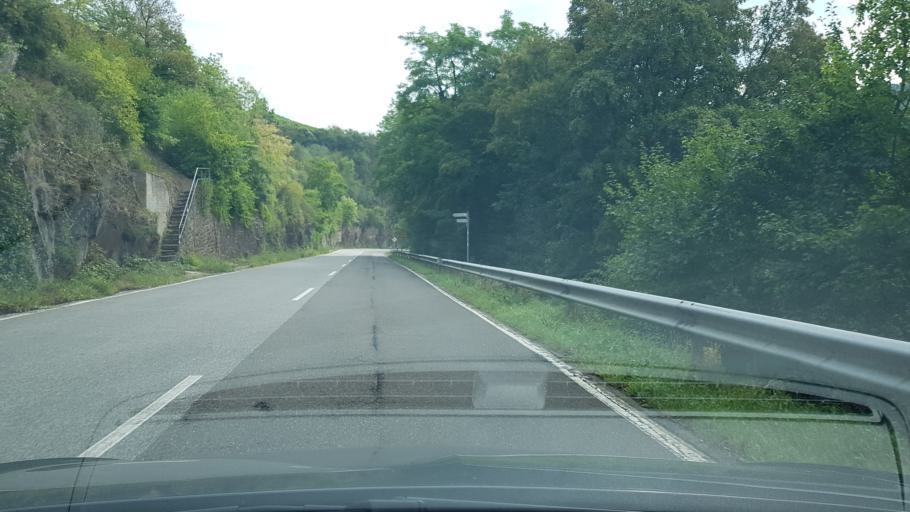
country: DE
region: Rheinland-Pfalz
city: Hatzenport
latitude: 50.2273
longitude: 7.4059
